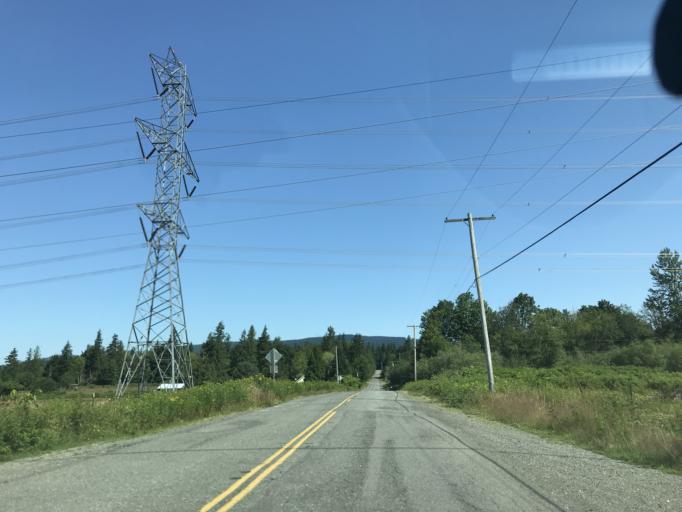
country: US
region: Washington
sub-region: King County
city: Ravensdale
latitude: 47.3628
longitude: -121.8801
